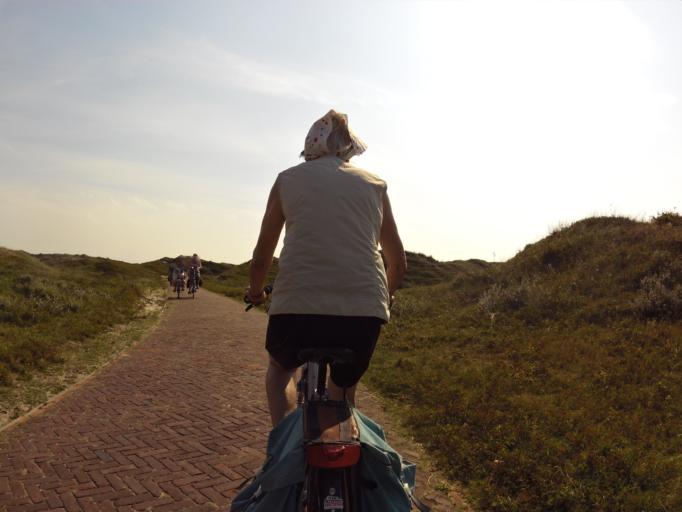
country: NL
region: North Holland
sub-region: Gemeente Bergen
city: Egmond aan Zee
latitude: 52.6546
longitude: 4.6311
